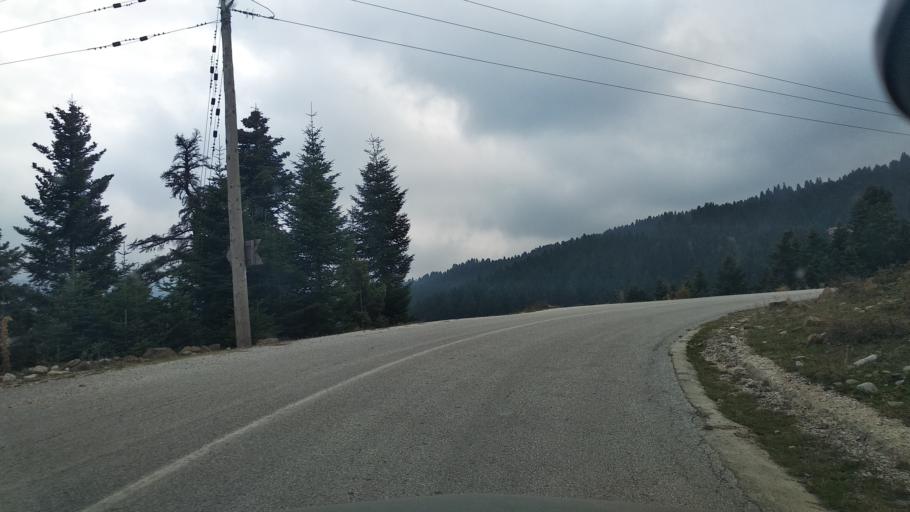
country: GR
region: Thessaly
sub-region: Trikala
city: Fiki
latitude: 39.5861
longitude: 21.4926
